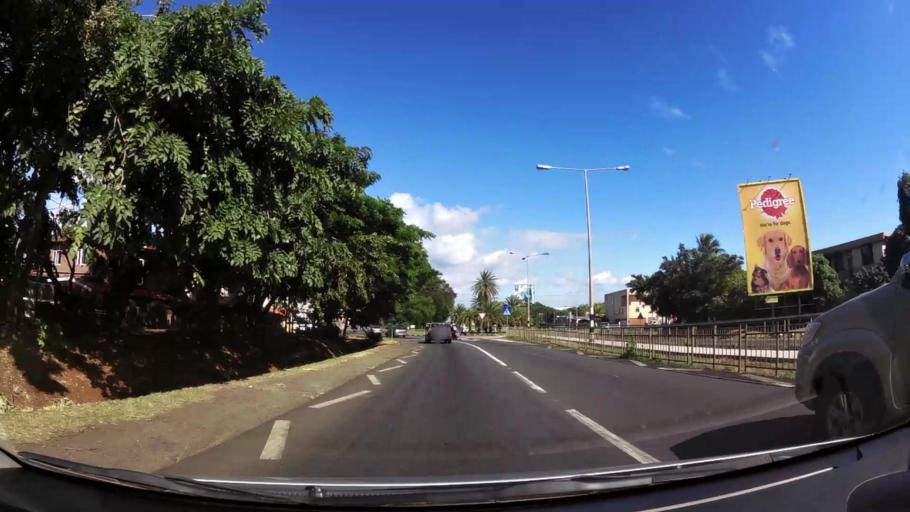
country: MU
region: Pamplemousses
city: Le Hochet
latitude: -20.1320
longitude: 57.5230
